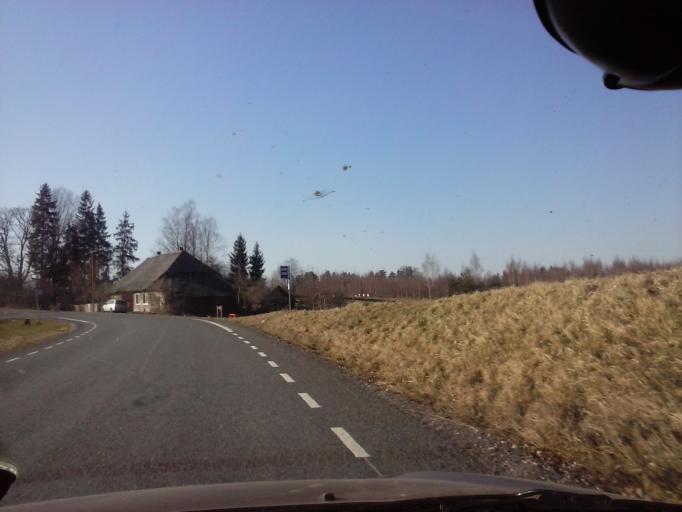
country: EE
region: Tartu
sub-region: UElenurme vald
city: Ulenurme
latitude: 58.1559
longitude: 26.8585
